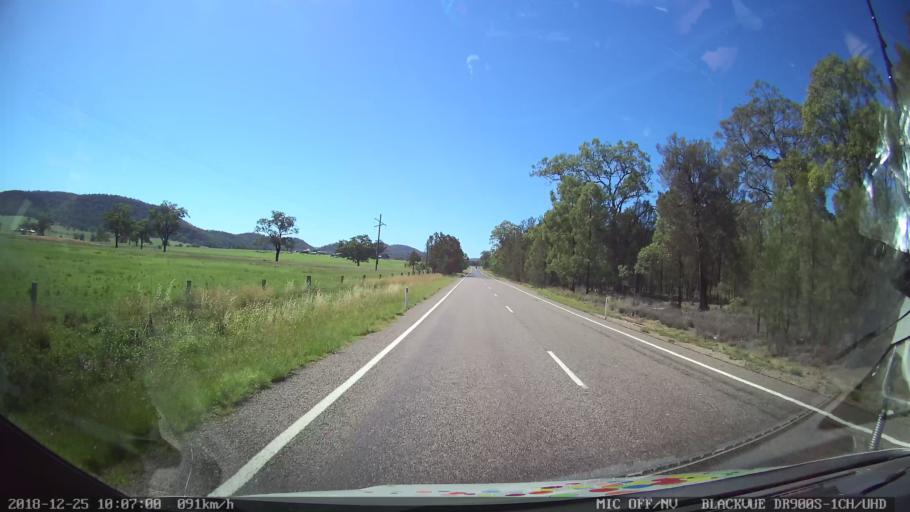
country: AU
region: New South Wales
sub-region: Upper Hunter Shire
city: Merriwa
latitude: -32.2661
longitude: 150.4944
